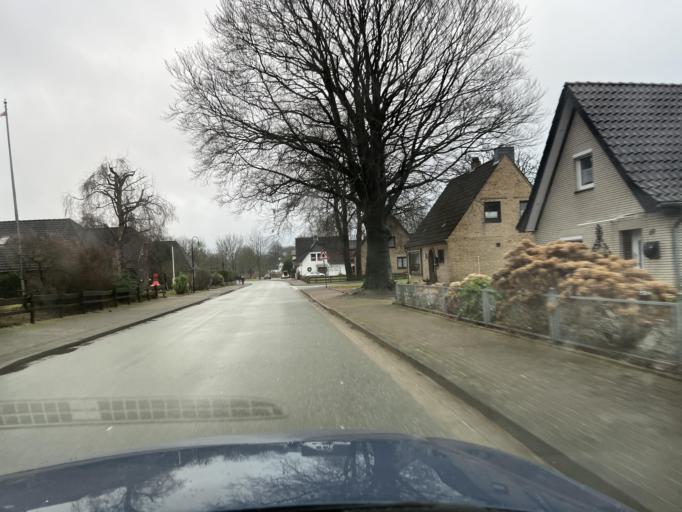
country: DE
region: Schleswig-Holstein
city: Wesseln
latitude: 54.2075
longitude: 9.0760
